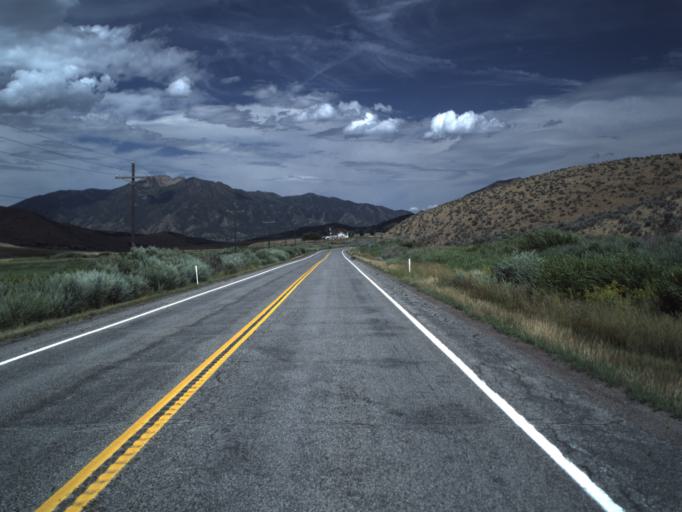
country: US
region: Utah
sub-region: Sanpete County
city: Fairview
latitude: 39.8241
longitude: -111.5096
